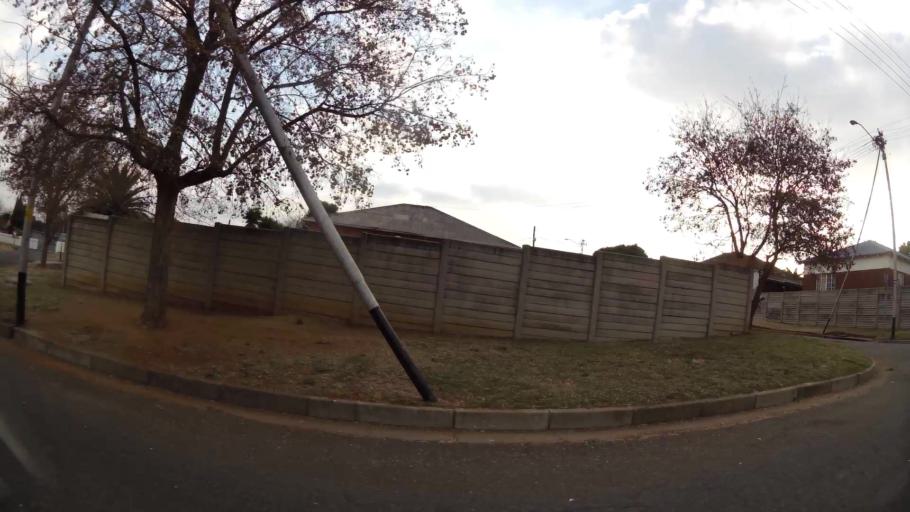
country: ZA
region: Gauteng
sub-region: Ekurhuleni Metropolitan Municipality
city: Germiston
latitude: -26.1793
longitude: 28.1770
